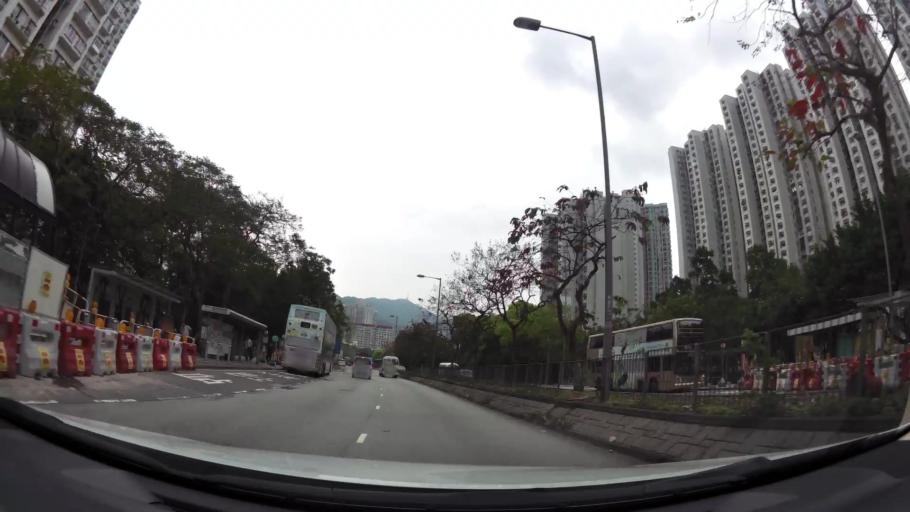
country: HK
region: Tai Po
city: Tai Po
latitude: 22.4529
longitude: 114.1724
